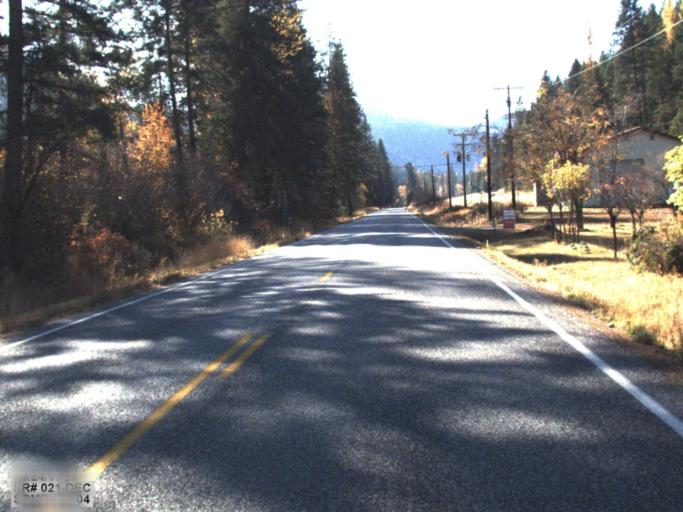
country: CA
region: British Columbia
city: Grand Forks
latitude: 48.9737
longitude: -118.5269
